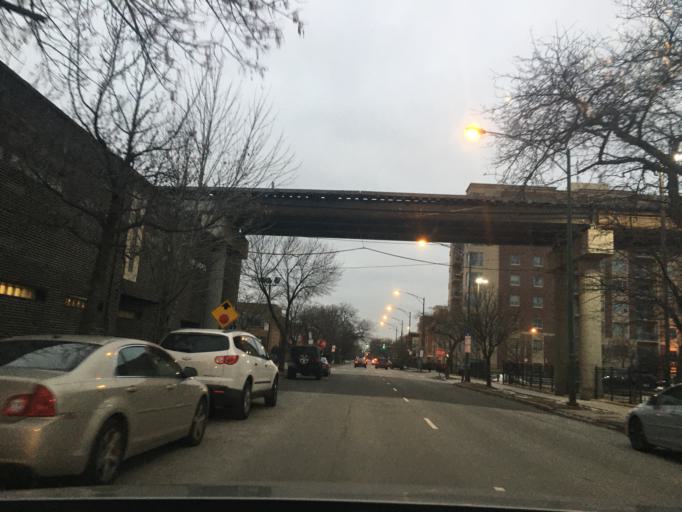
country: US
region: Illinois
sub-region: Cook County
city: Chicago
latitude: 41.8833
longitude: -87.6697
